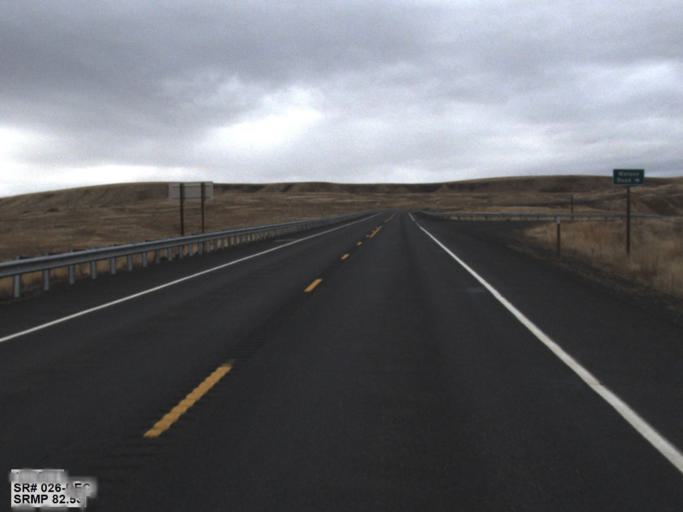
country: US
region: Washington
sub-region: Adams County
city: Ritzville
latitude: 46.7588
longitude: -118.3175
